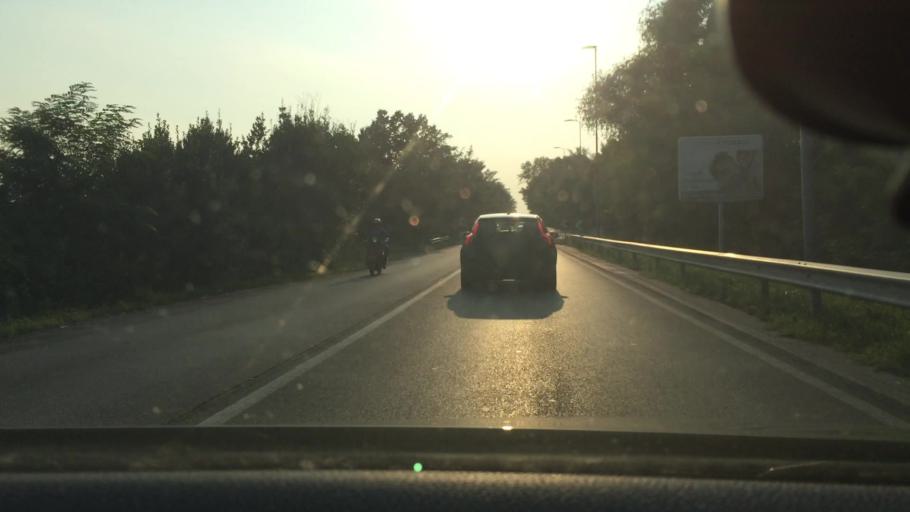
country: IT
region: Lombardy
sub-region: Provincia di Bergamo
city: Lallio
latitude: 45.6896
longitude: 9.6378
